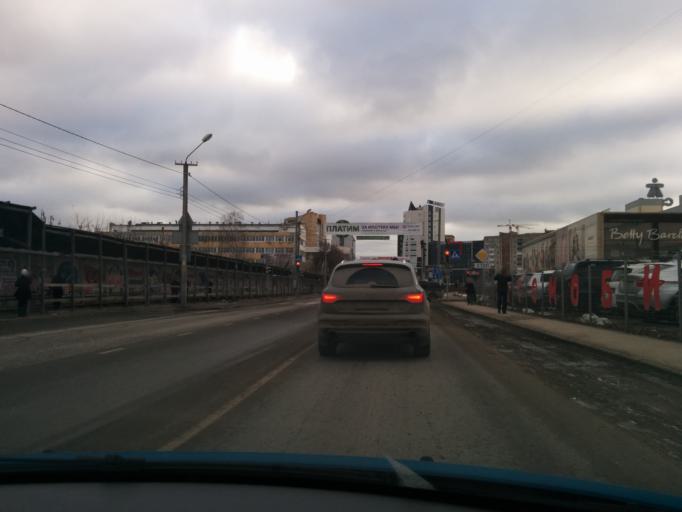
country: RU
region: Perm
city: Perm
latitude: 58.0089
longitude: 56.2627
